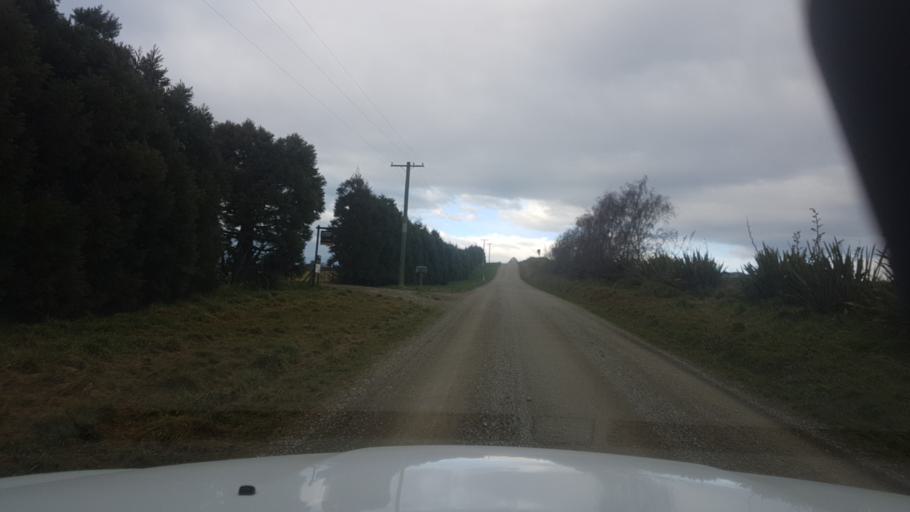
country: NZ
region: Canterbury
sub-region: Timaru District
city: Pleasant Point
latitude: -44.3490
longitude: 171.1561
